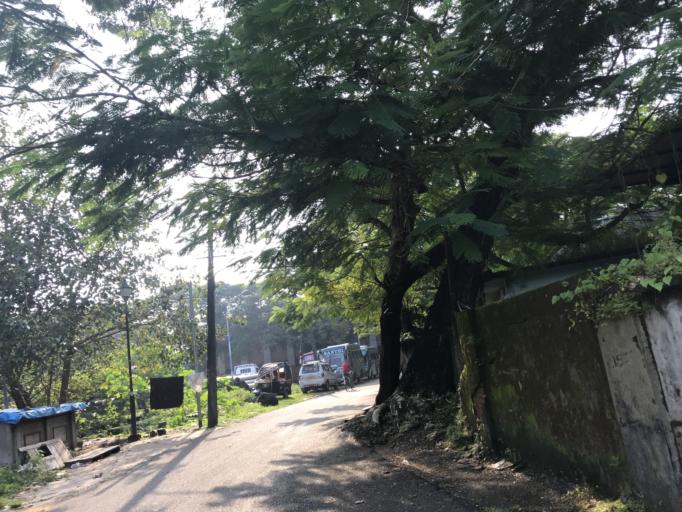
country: IN
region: Kerala
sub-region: Ernakulam
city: Cochin
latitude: 9.9655
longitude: 76.2462
